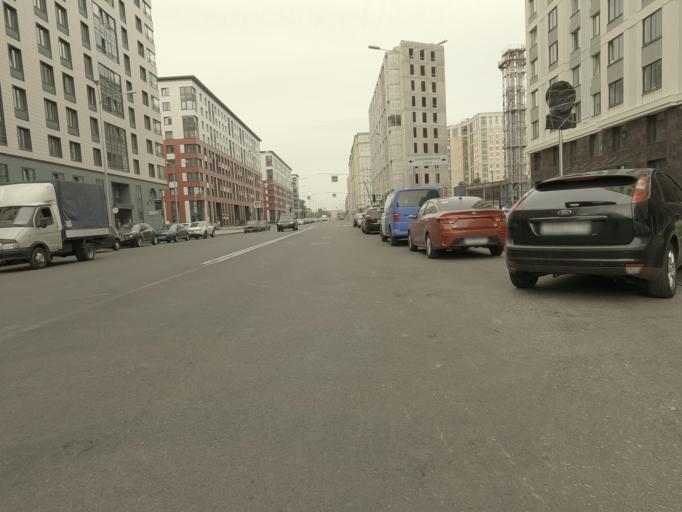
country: RU
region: St.-Petersburg
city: Admiralteisky
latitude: 59.9008
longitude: 30.3121
